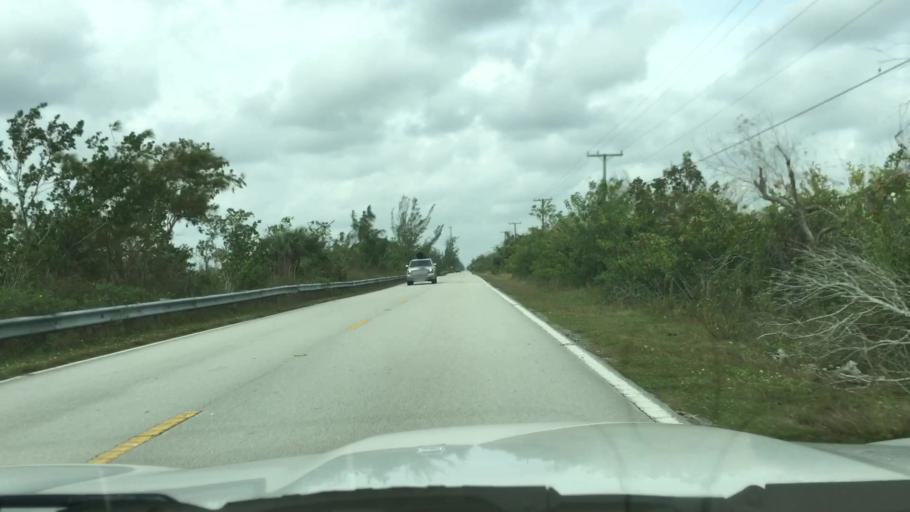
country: US
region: Florida
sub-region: Miami-Dade County
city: Florida City
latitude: 25.3681
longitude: -80.4305
